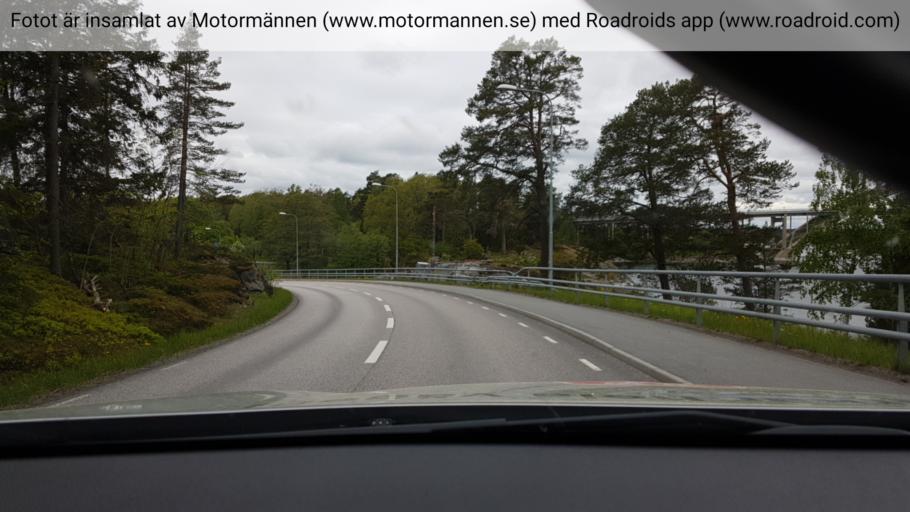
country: SE
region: Stockholm
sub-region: Varmdo Kommun
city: Holo
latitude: 59.2915
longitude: 18.6731
